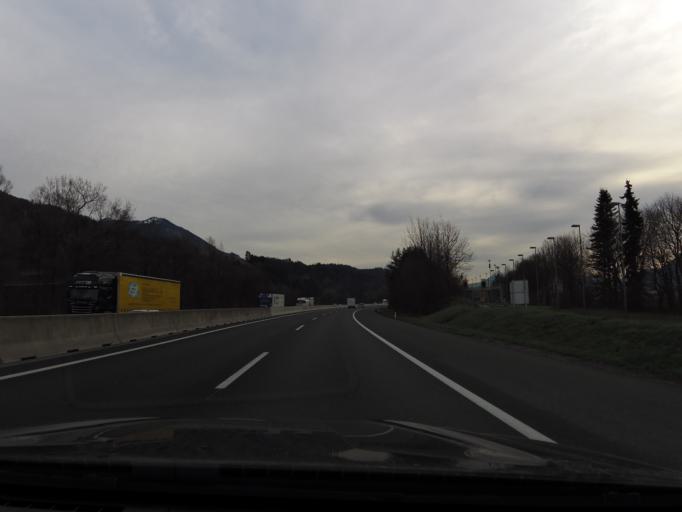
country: AT
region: Tyrol
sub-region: Politischer Bezirk Kufstein
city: Radfeld
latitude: 47.4561
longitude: 11.9159
